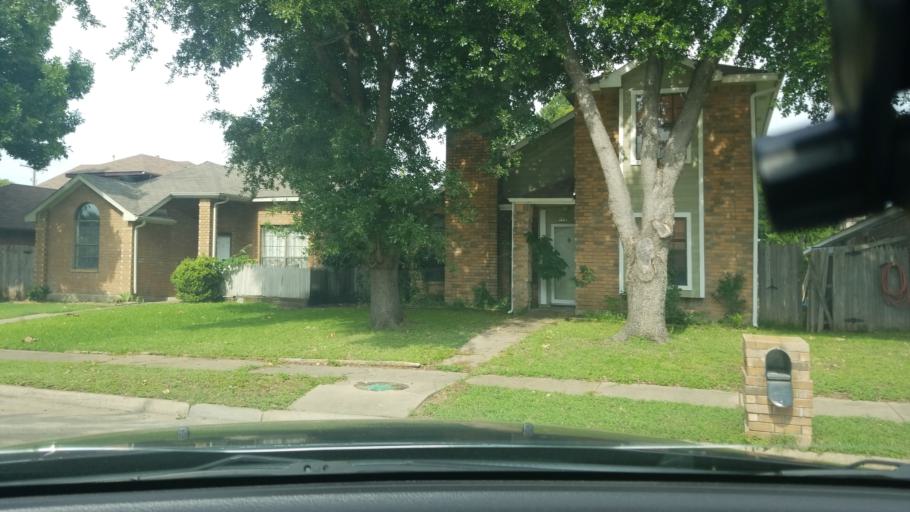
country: US
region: Texas
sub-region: Dallas County
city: Balch Springs
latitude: 32.7567
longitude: -96.6279
